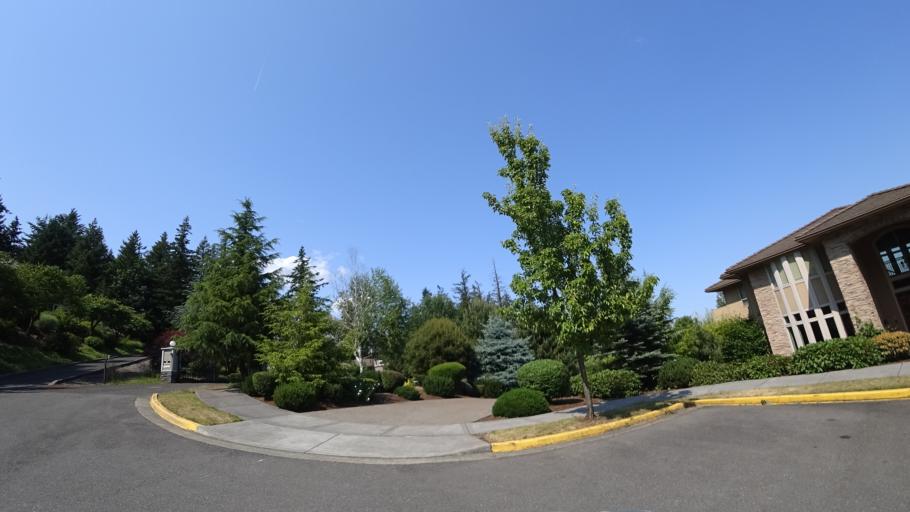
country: US
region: Oregon
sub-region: Clackamas County
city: Happy Valley
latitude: 45.4478
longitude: -122.5386
